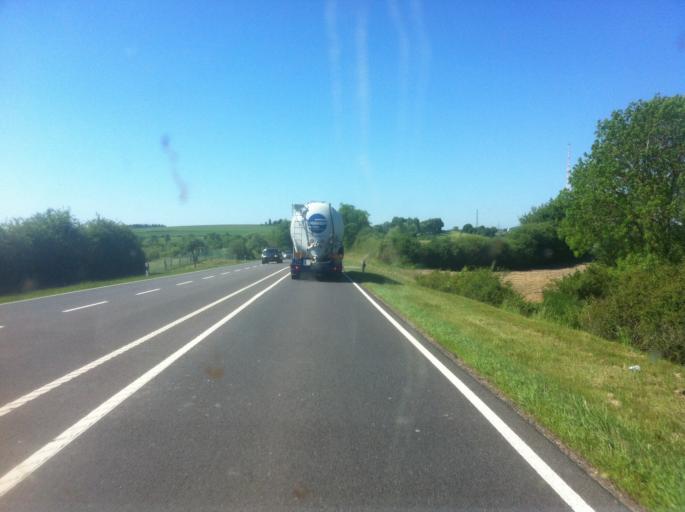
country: LU
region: Grevenmacher
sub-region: Canton de Grevenmacher
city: Junglinster
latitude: 49.7301
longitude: 6.2824
